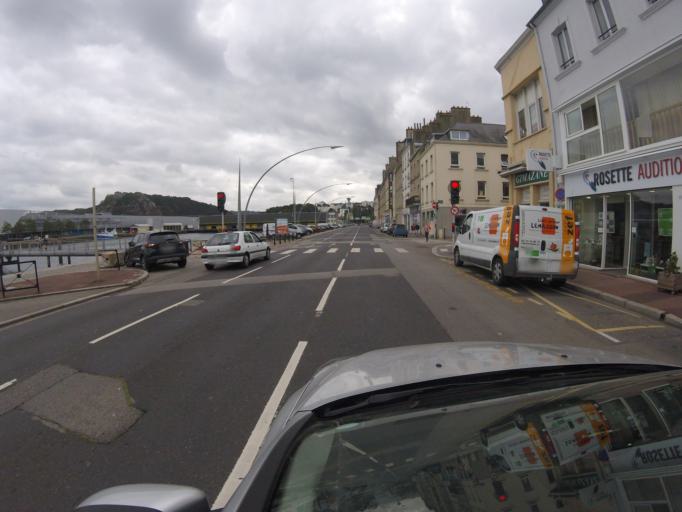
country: FR
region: Lower Normandy
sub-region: Departement de la Manche
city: Cherbourg-Octeville
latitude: 49.6372
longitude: -1.6217
